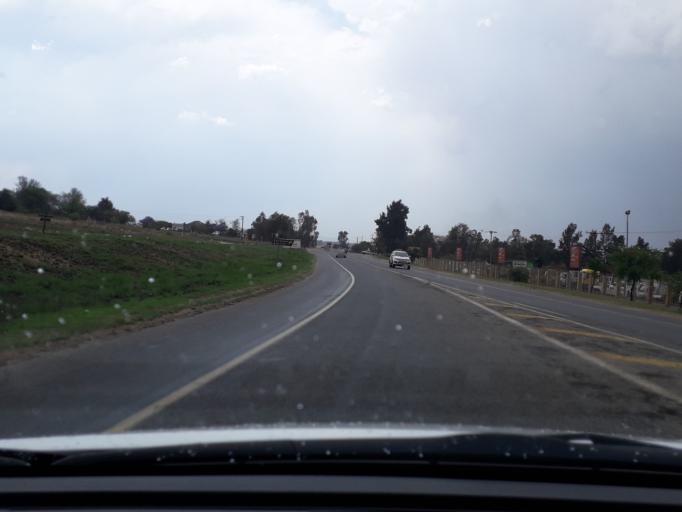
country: ZA
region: Gauteng
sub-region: West Rand District Municipality
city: Muldersdriseloop
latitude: -26.0160
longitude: 27.8590
